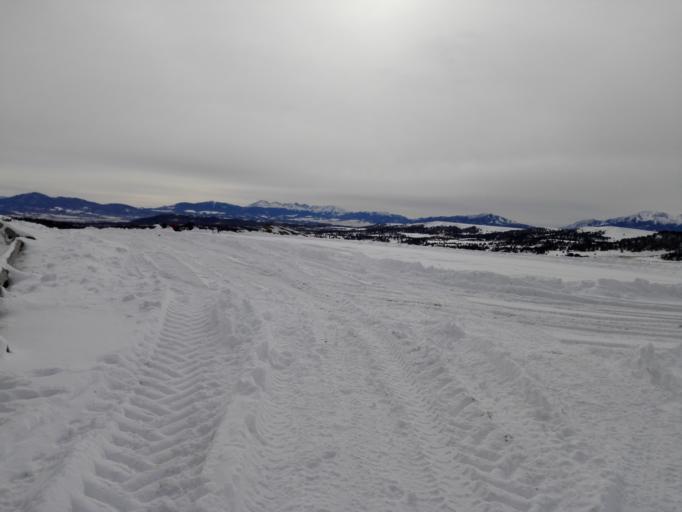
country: US
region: Colorado
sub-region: Custer County
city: Westcliffe
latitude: 37.9630
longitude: -105.2154
